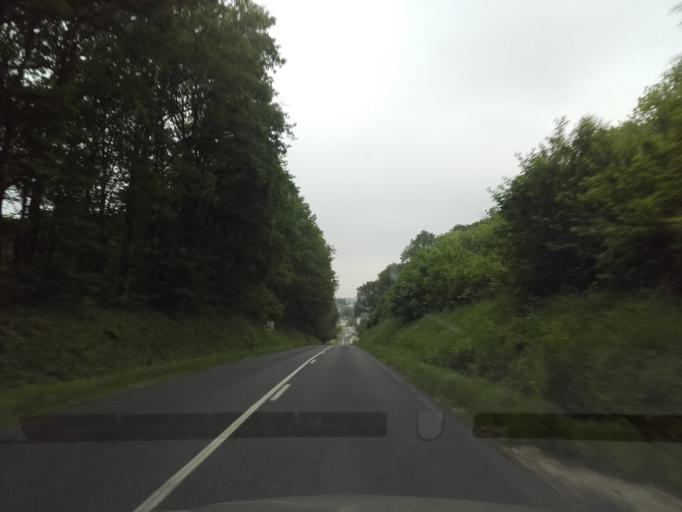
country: FR
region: Centre
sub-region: Departement d'Indre-et-Loire
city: Cerelles
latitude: 47.5007
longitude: 0.6970
